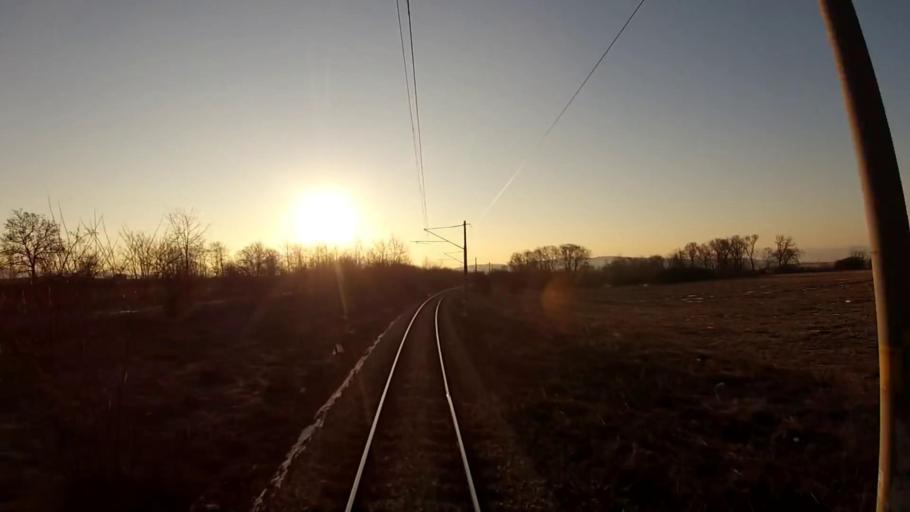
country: BG
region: Sofiya
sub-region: Obshtina Dragoman
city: Dragoman
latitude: 42.8846
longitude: 22.9806
